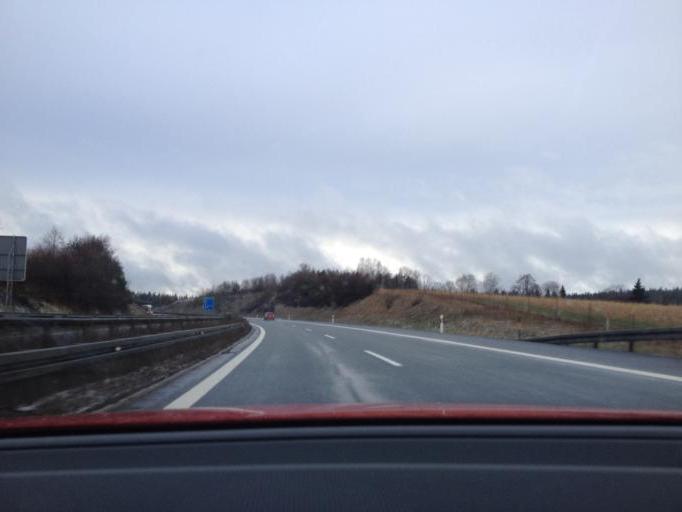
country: DE
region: Bavaria
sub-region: Upper Franconia
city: Schonwald
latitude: 50.2120
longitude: 12.1061
